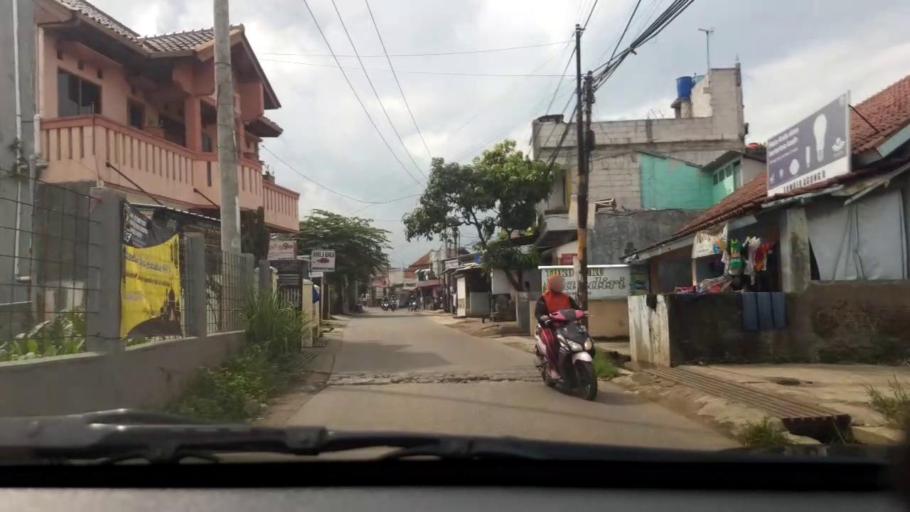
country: ID
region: West Java
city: Cileunyi
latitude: -6.9409
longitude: 107.7215
